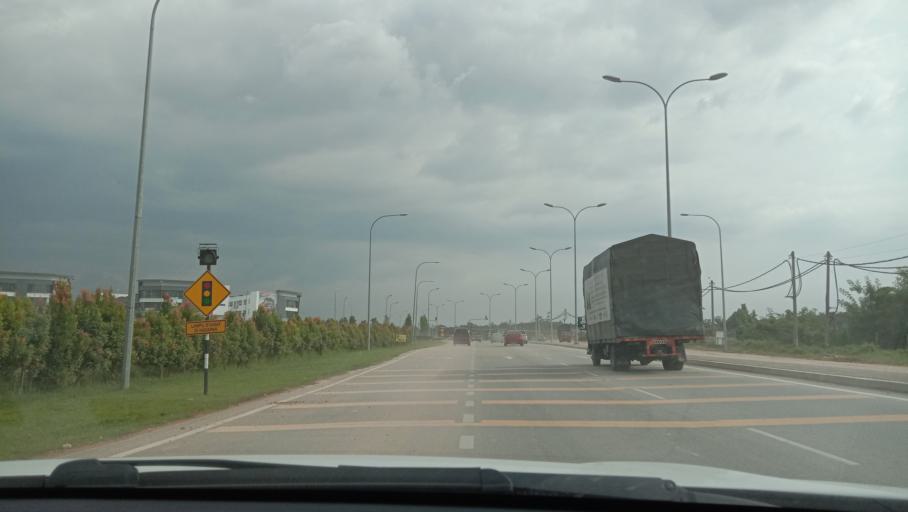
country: MY
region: Selangor
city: Ladang Seri Kundang
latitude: 3.2445
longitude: 101.4734
